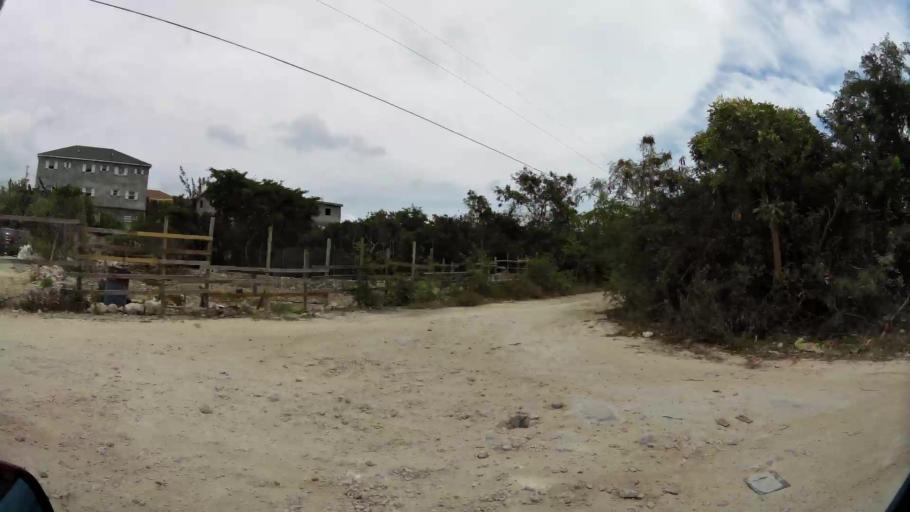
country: BS
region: Mayaguana
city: Abraham's Bay
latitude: 21.7854
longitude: -72.2587
